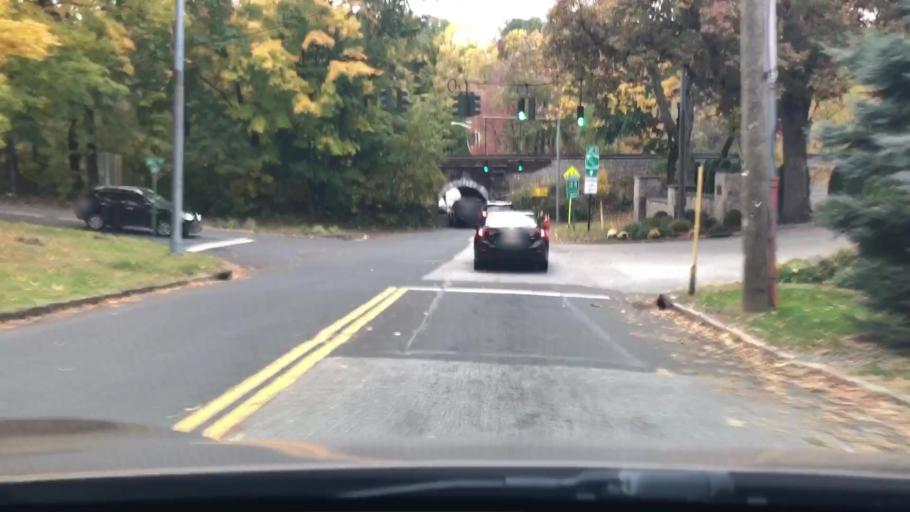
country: US
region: New York
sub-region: Westchester County
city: Tuckahoe
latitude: 40.9686
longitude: -73.8156
